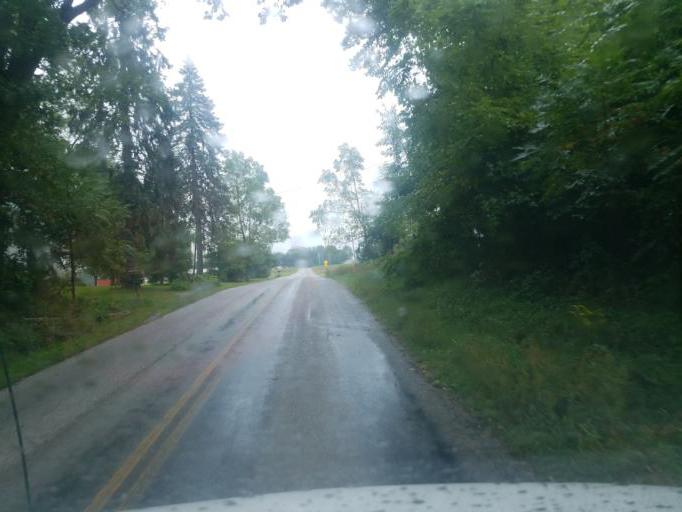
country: US
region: Ohio
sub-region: Medina County
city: Seville
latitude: 40.9823
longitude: -81.8348
